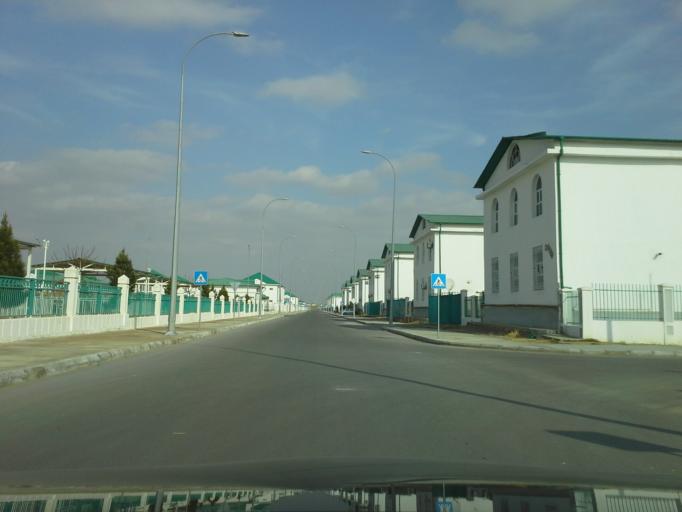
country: TM
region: Ahal
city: Abadan
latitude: 38.0775
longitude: 58.2736
